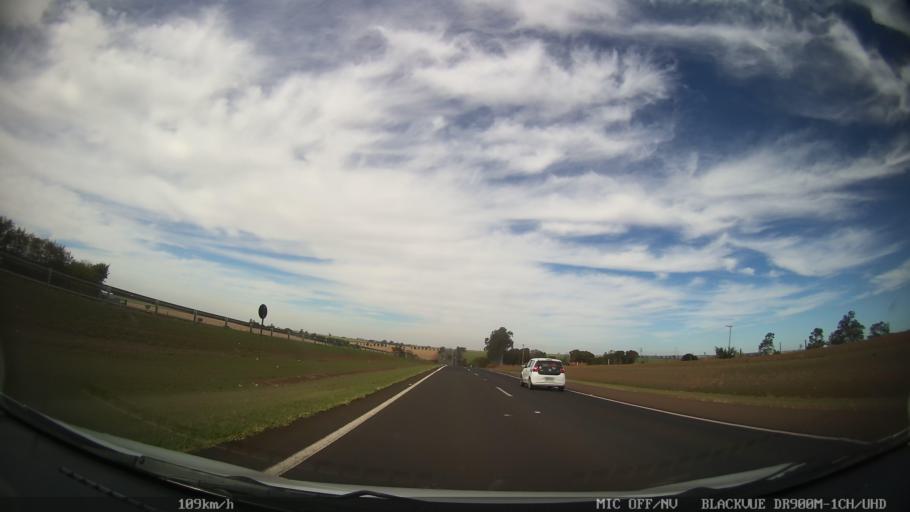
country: BR
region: Sao Paulo
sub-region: Taquaritinga
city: Taquaritinga
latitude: -21.5036
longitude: -48.5582
